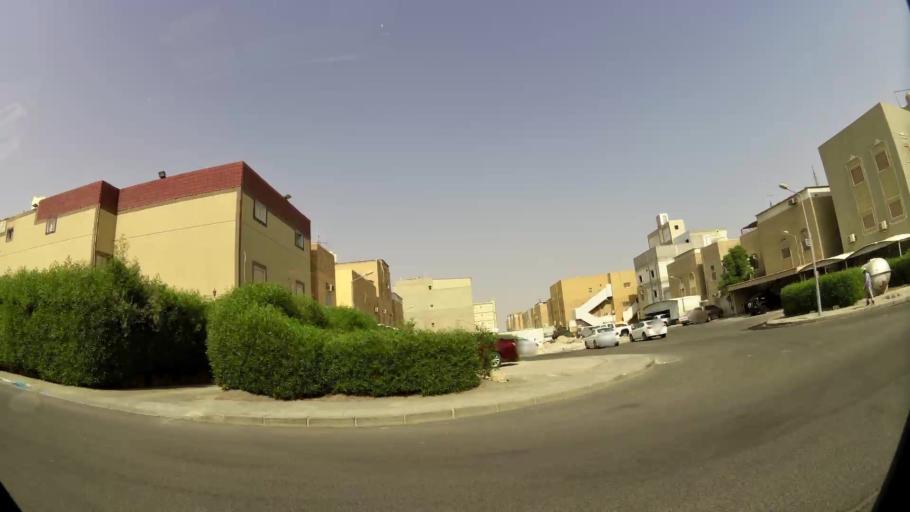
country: KW
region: Muhafazat al Jahra'
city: Al Jahra'
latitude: 29.3339
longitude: 47.6575
